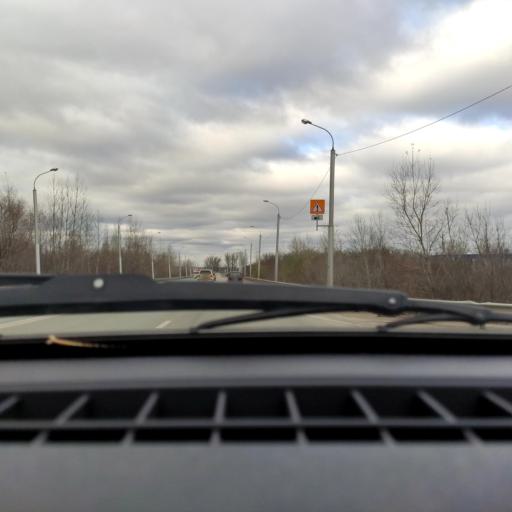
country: RU
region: Bashkortostan
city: Iglino
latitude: 54.7947
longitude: 56.2090
